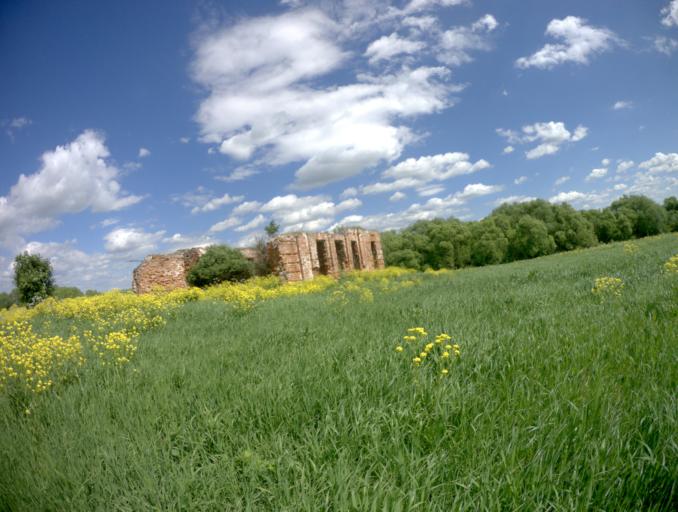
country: RU
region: Ivanovo
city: Gavrilov Posad
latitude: 56.4415
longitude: 40.2484
